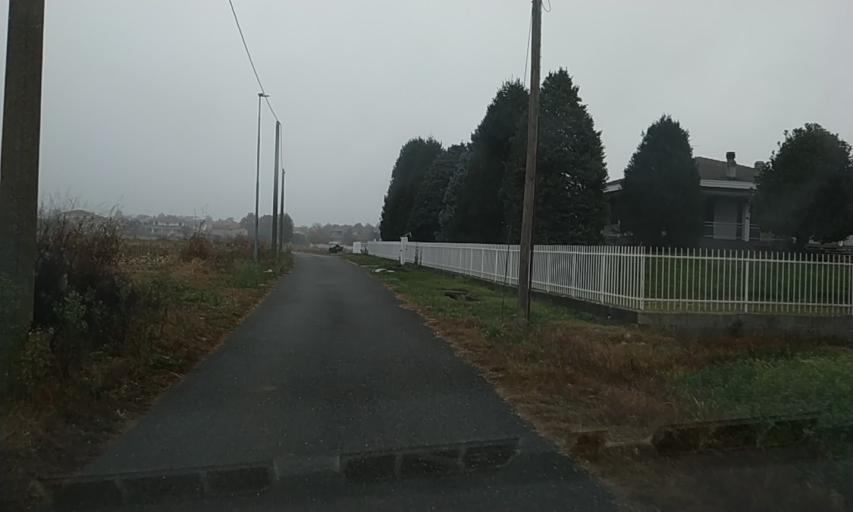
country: IT
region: Piedmont
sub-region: Provincia di Vercelli
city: Alice Castello
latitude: 45.3664
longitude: 8.0663
